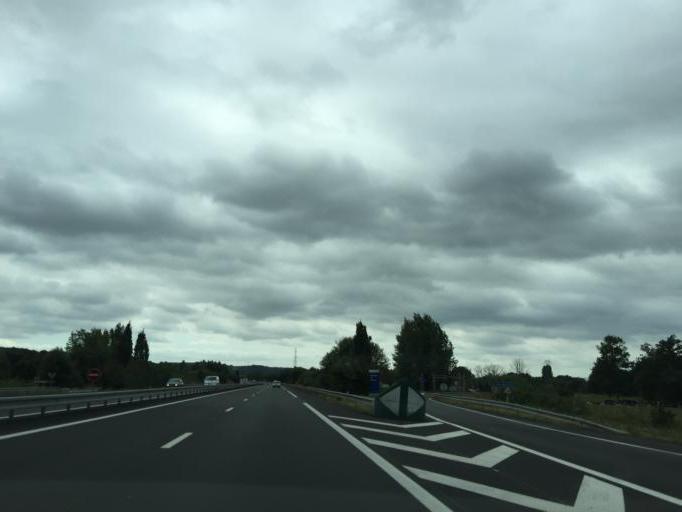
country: FR
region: Pays de la Loire
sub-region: Departement de la Sarthe
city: Teloche
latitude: 47.8848
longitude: 0.3046
